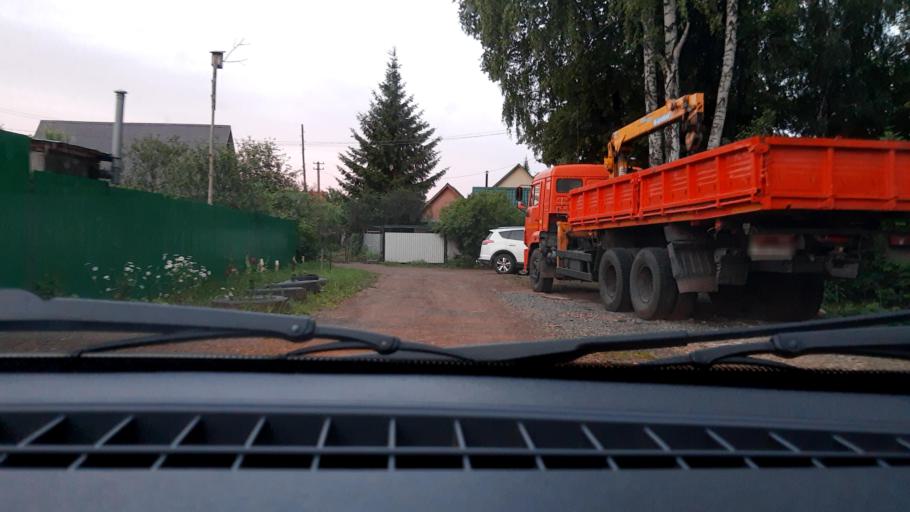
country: RU
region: Bashkortostan
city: Mikhaylovka
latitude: 54.8005
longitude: 55.7704
